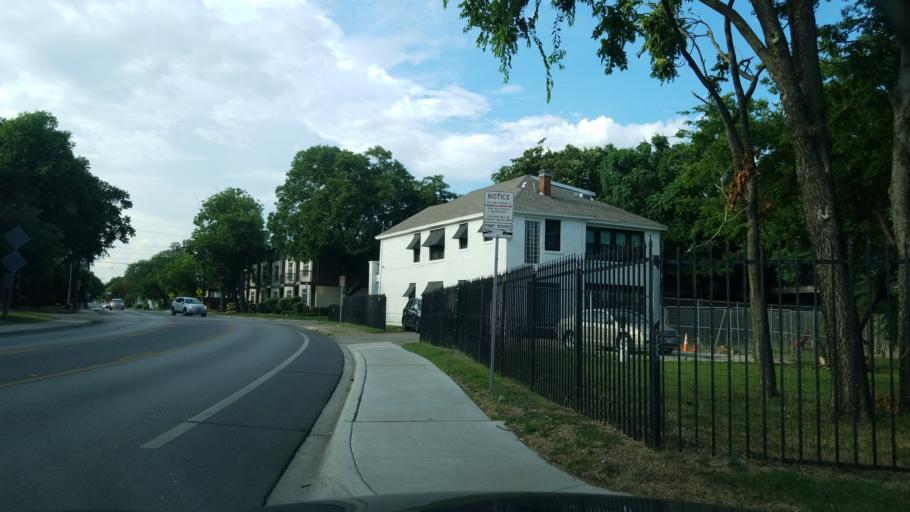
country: US
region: Texas
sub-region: Dallas County
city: Highland Park
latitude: 32.8133
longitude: -96.7681
